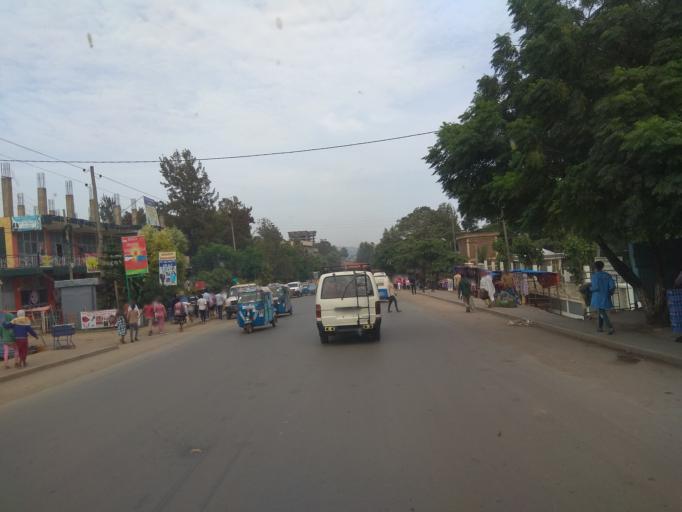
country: ET
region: Oromiya
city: Hagere Hiywet
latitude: 8.9821
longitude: 37.8511
